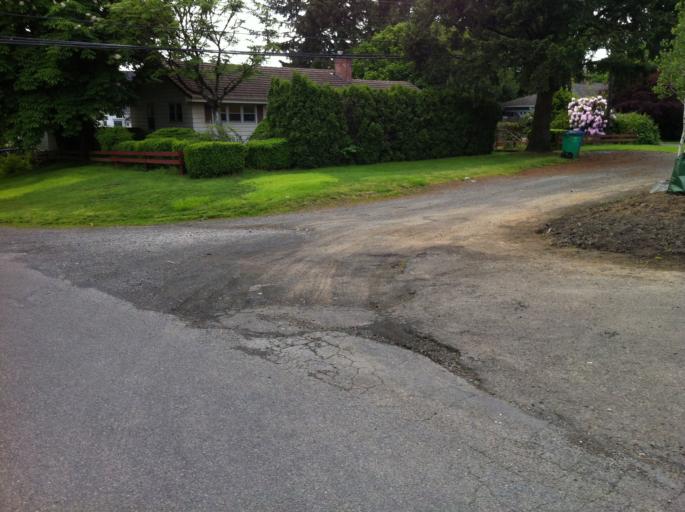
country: US
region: Oregon
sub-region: Clackamas County
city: Lake Oswego
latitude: 45.4645
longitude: -122.6855
